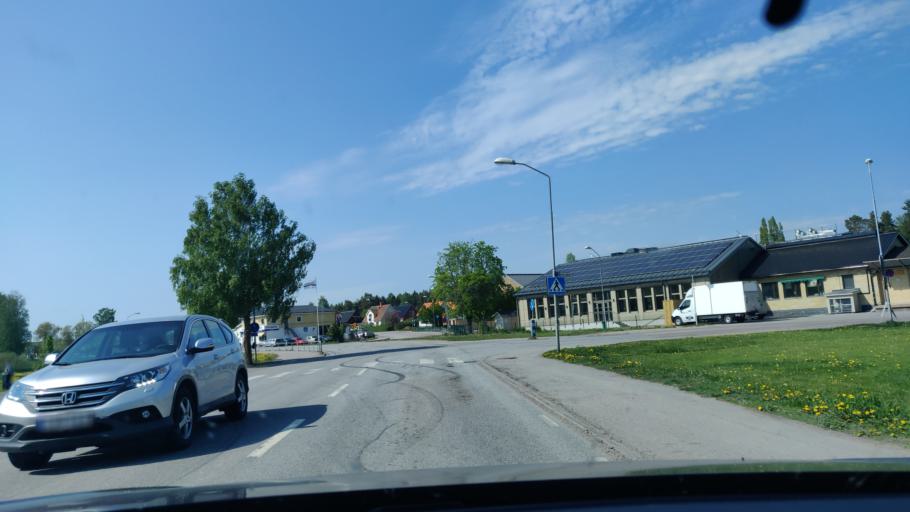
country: SE
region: Uppsala
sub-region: Heby Kommun
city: OEstervala
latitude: 60.1815
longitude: 17.1752
